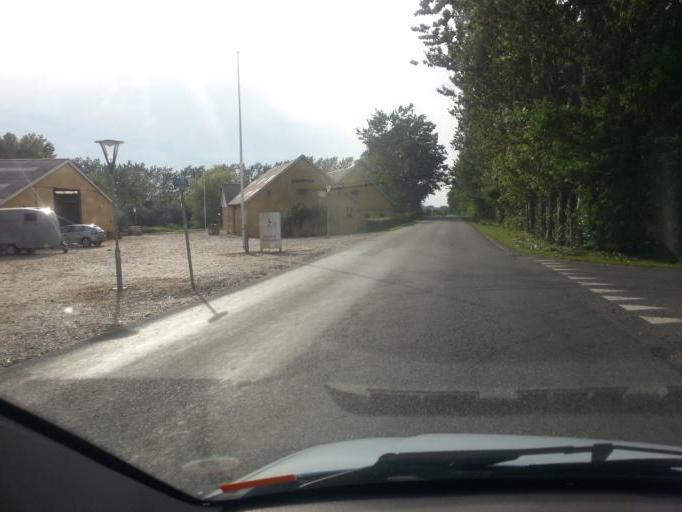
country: DK
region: South Denmark
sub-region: Vejen Kommune
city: Holsted
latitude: 55.4910
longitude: 8.9363
